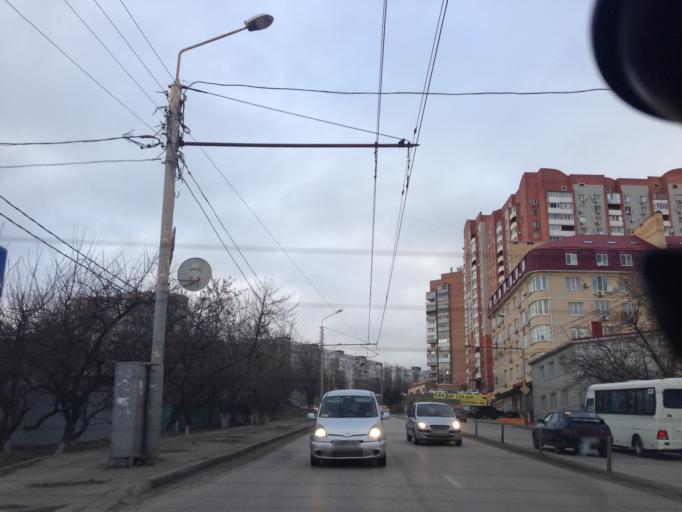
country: RU
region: Rostov
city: Severnyy
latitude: 47.2969
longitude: 39.7261
